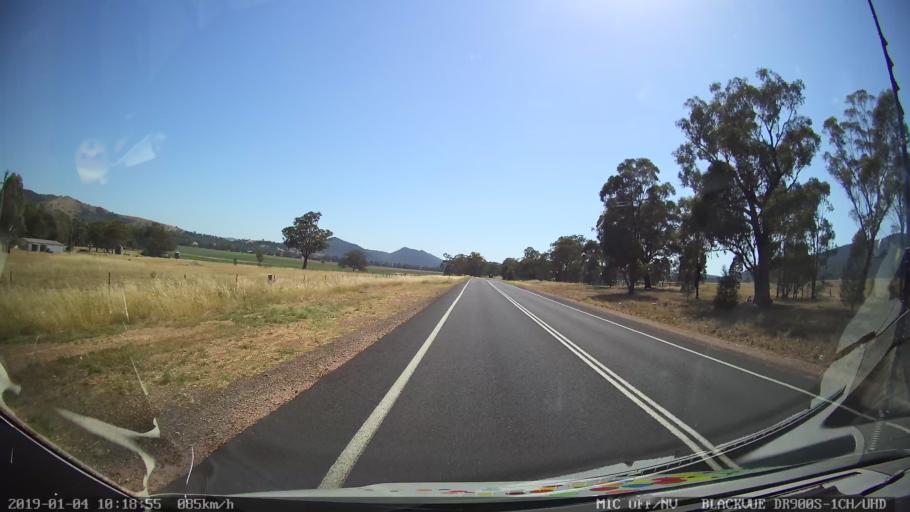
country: AU
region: New South Wales
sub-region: Cabonne
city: Canowindra
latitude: -33.3794
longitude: 148.4733
